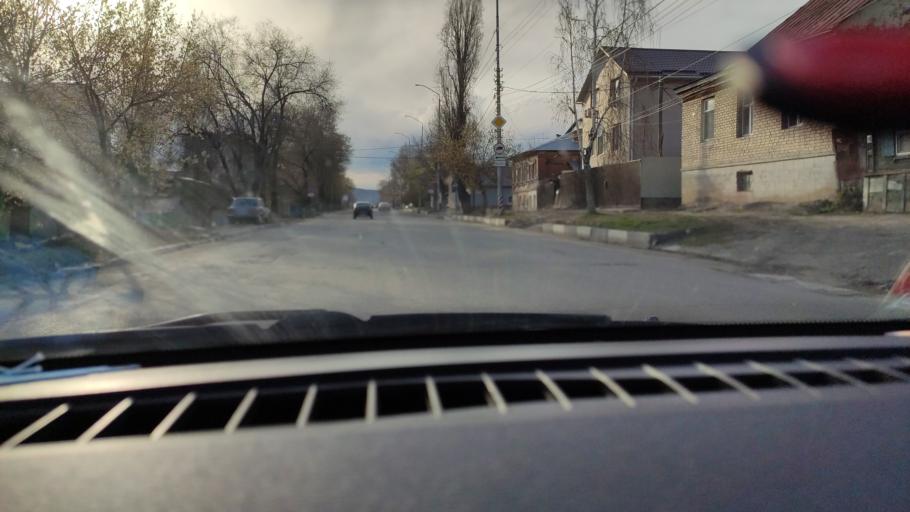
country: RU
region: Saratov
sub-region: Saratovskiy Rayon
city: Saratov
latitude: 51.5400
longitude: 46.0499
